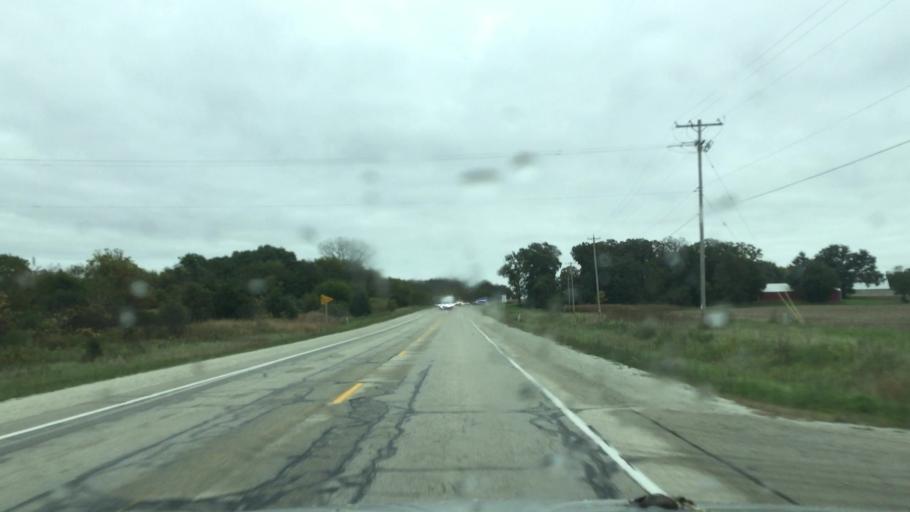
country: US
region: Wisconsin
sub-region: Racine County
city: Eagle Lake
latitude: 42.7426
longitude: -88.1502
